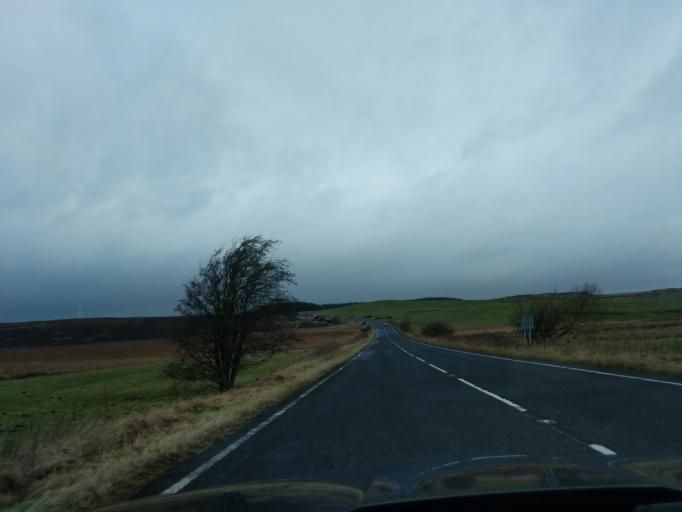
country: GB
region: England
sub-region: Northumberland
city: Rothley
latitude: 55.1711
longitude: -2.0240
